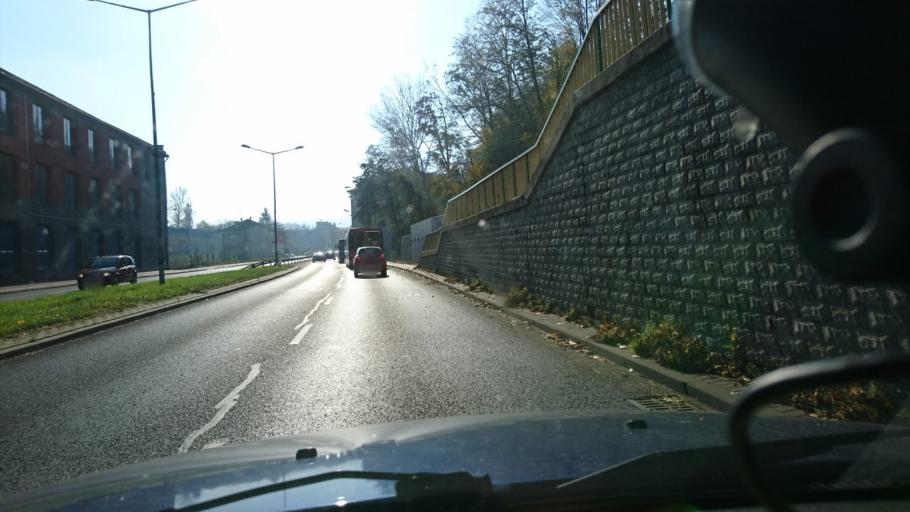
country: PL
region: Silesian Voivodeship
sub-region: Bielsko-Biala
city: Bielsko-Biala
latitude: 49.8068
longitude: 19.0429
